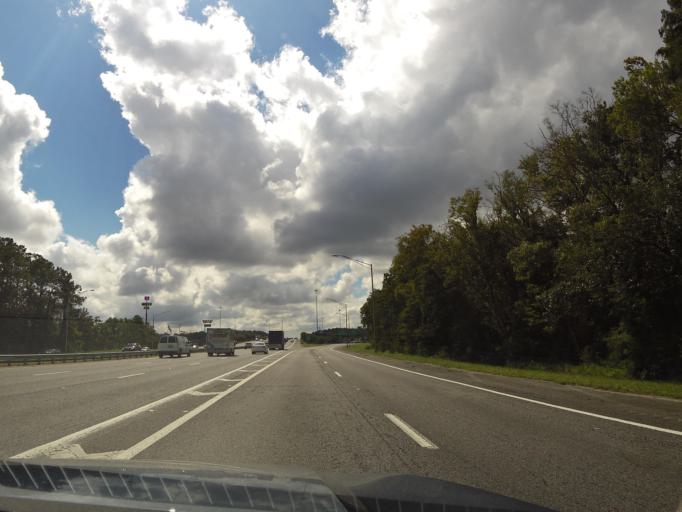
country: US
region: Florida
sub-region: Saint Johns County
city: Fruit Cove
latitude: 30.0707
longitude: -81.4990
